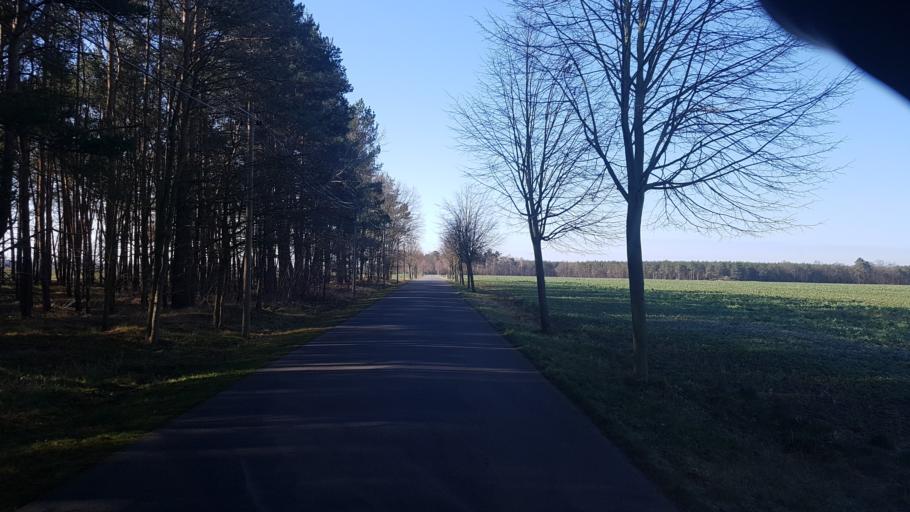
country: DE
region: Brandenburg
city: Luckau
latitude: 51.8340
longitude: 13.7891
